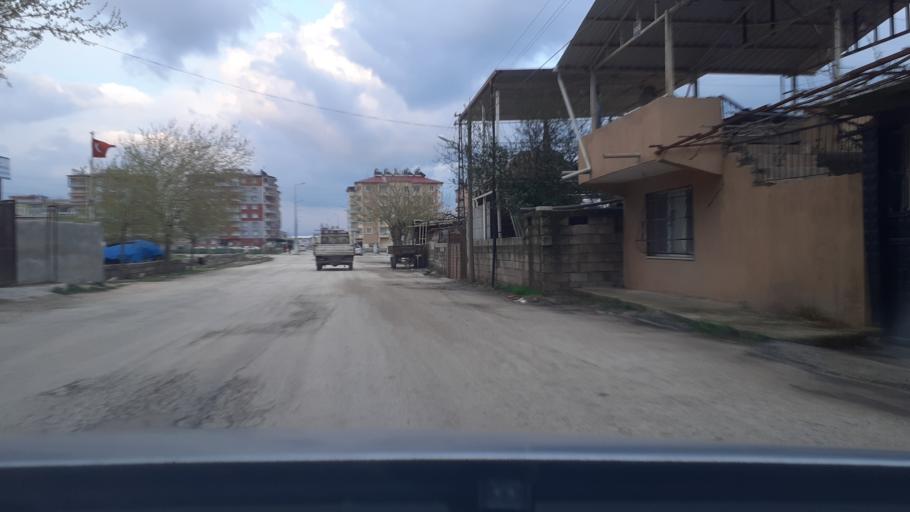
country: TR
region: Hatay
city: Kirikhan
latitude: 36.4833
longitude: 36.3511
